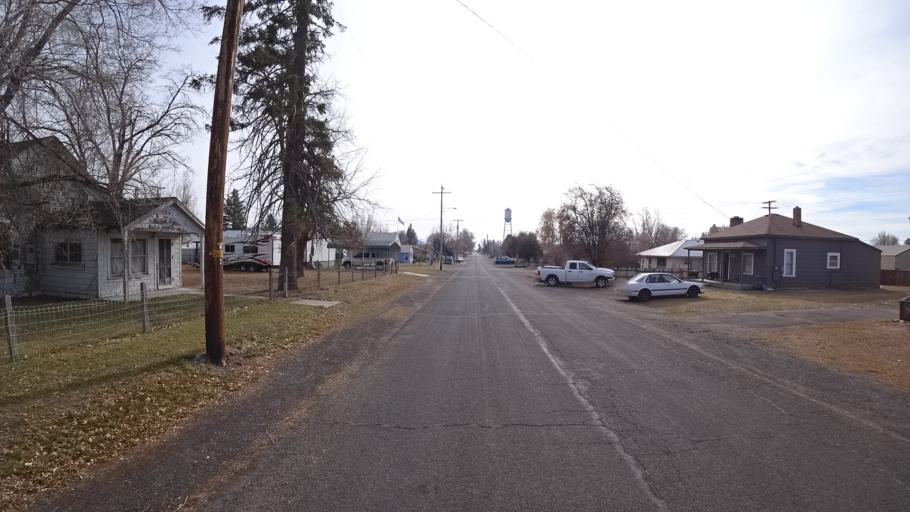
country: US
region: Oregon
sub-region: Klamath County
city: Klamath Falls
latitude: 41.9691
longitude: -121.9196
